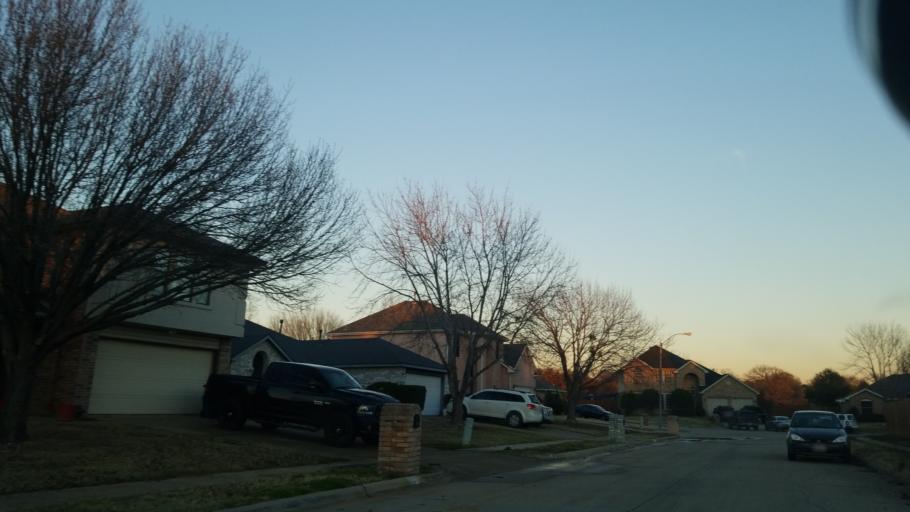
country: US
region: Texas
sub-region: Denton County
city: Corinth
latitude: 33.1386
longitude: -97.0694
